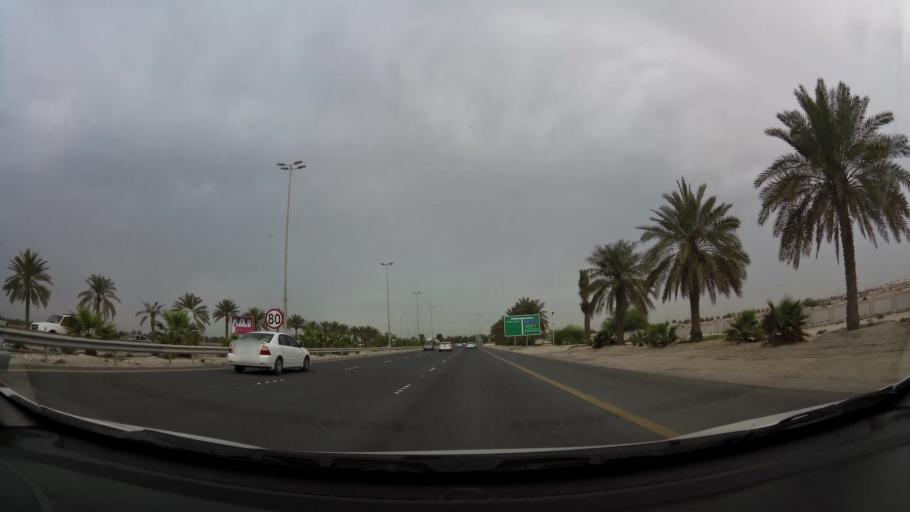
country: BH
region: Central Governorate
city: Dar Kulayb
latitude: 26.0532
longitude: 50.4999
